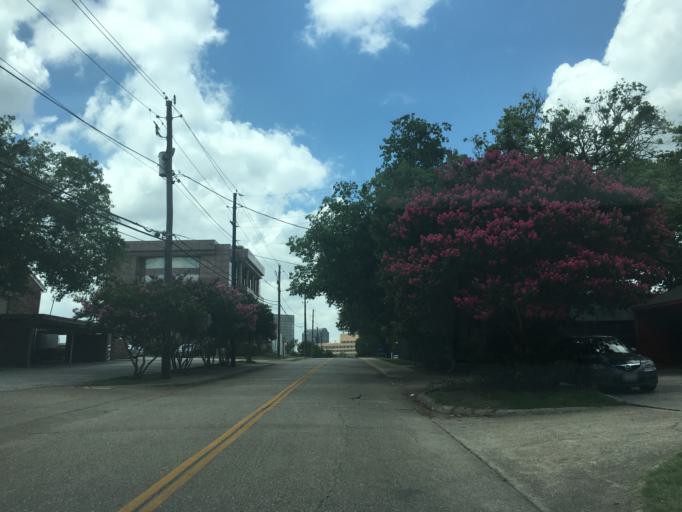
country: US
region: Texas
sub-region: Dallas County
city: University Park
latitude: 32.8761
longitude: -96.7593
